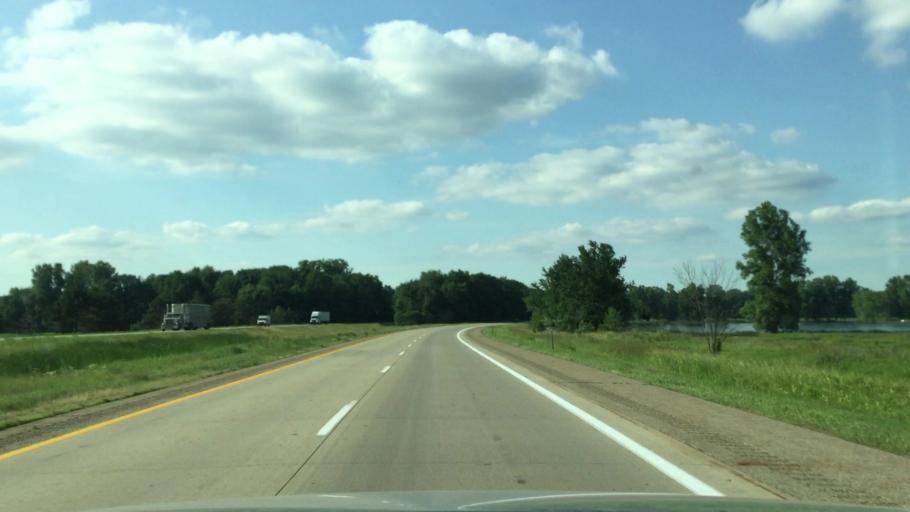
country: US
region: Michigan
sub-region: Calhoun County
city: Marshall
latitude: 42.1330
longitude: -84.9952
